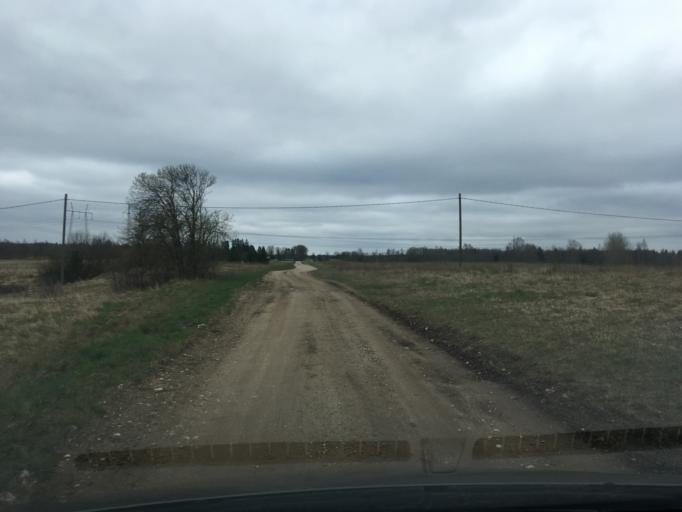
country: EE
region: Harju
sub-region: Raasiku vald
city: Arukula
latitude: 59.2749
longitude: 25.1157
